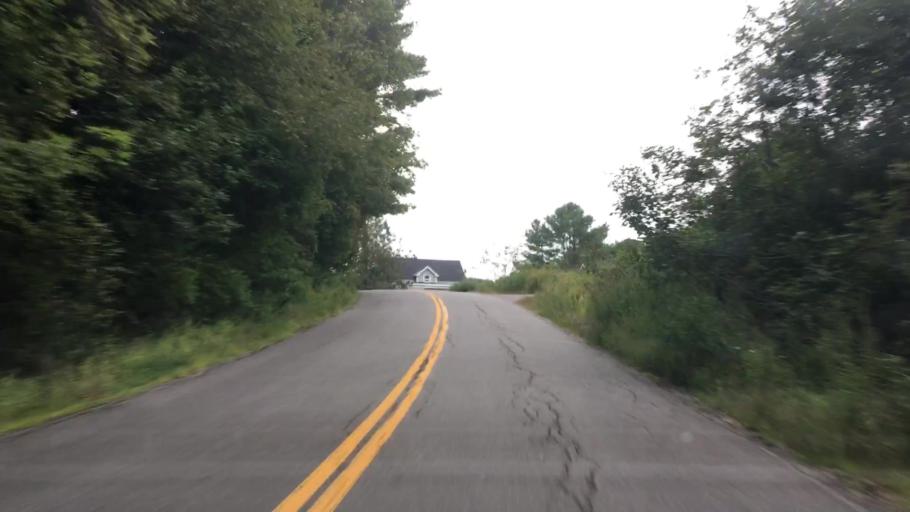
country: US
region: Maine
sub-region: Cumberland County
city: New Gloucester
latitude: 43.9071
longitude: -70.2206
